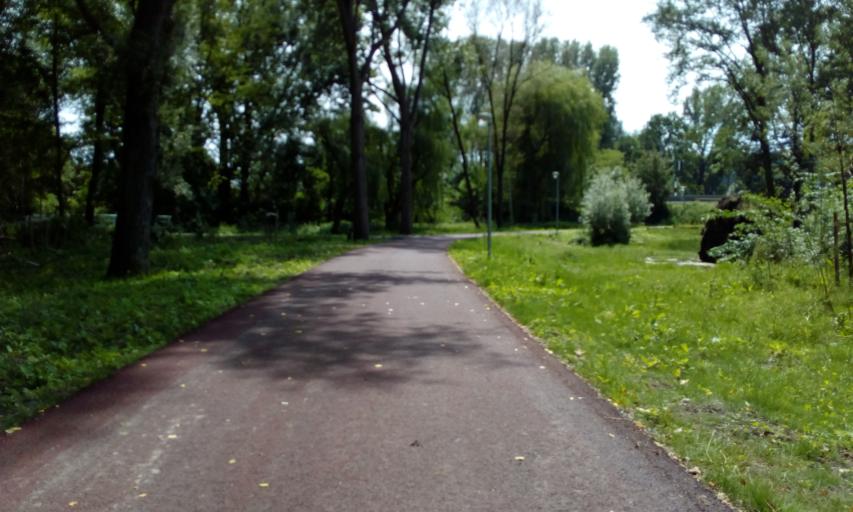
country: NL
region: South Holland
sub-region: Gemeente Schiedam
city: Schiedam
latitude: 51.9261
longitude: 4.3884
